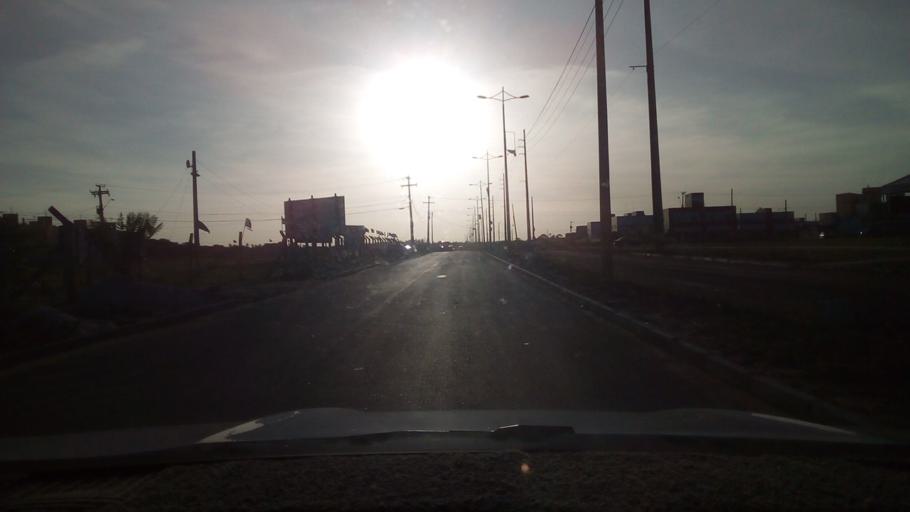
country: BR
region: Paraiba
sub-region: Conde
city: Conde
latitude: -7.1994
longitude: -34.8716
